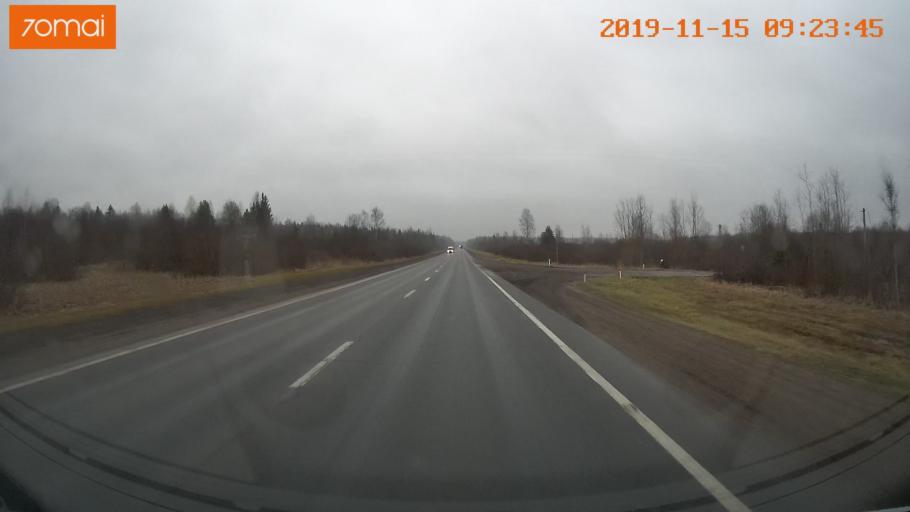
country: RU
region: Vologda
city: Tonshalovo
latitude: 59.3019
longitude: 38.1202
